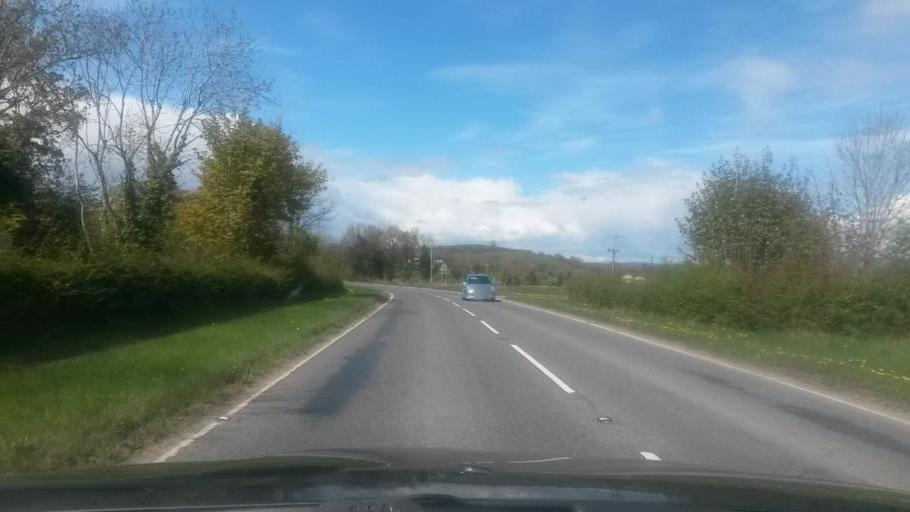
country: GB
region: Northern Ireland
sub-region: Fermanagh District
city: Enniskillen
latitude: 54.3664
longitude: -7.6796
